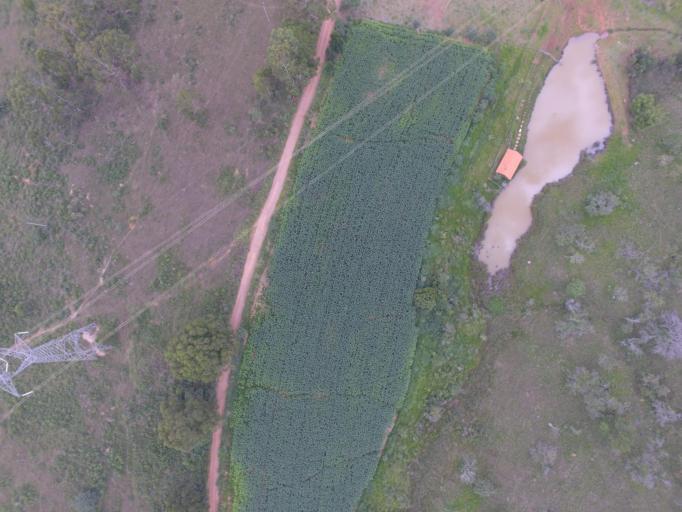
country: BR
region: Minas Gerais
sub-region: Tiradentes
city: Tiradentes
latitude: -21.0456
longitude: -44.0857
